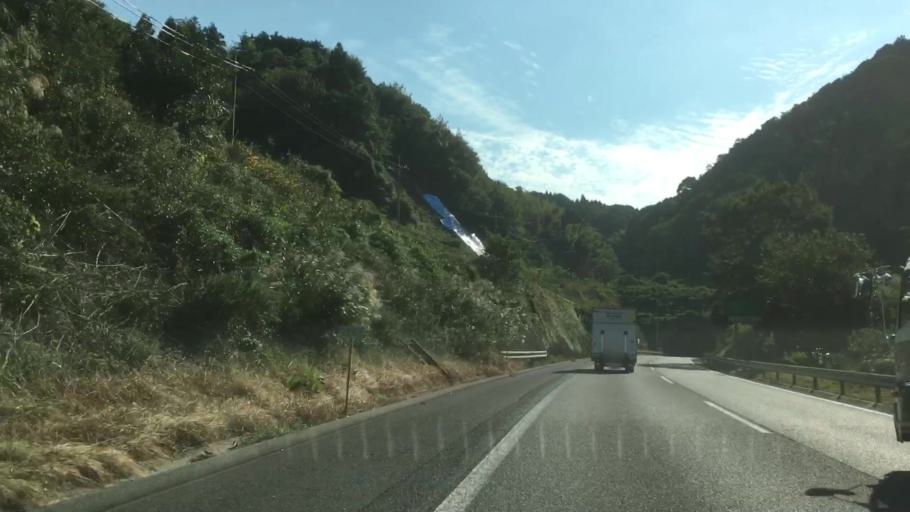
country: JP
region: Yamaguchi
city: Otake
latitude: 34.2321
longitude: 132.2123
